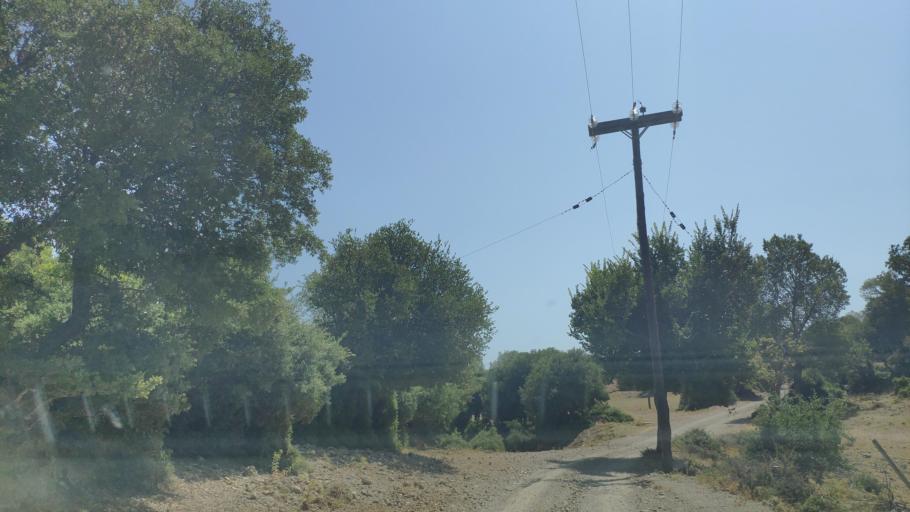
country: GR
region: West Greece
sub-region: Nomos Aitolias kai Akarnanias
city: Monastirakion
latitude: 38.8170
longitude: 21.0212
